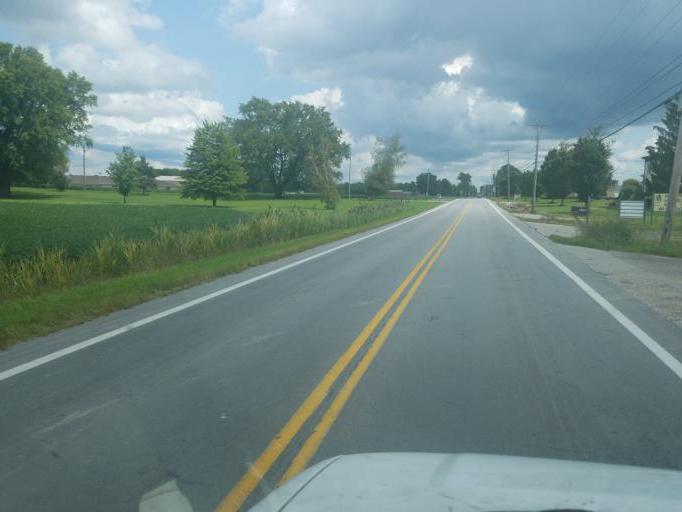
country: US
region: Ohio
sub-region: Ashtabula County
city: Andover
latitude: 41.6071
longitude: -80.5925
